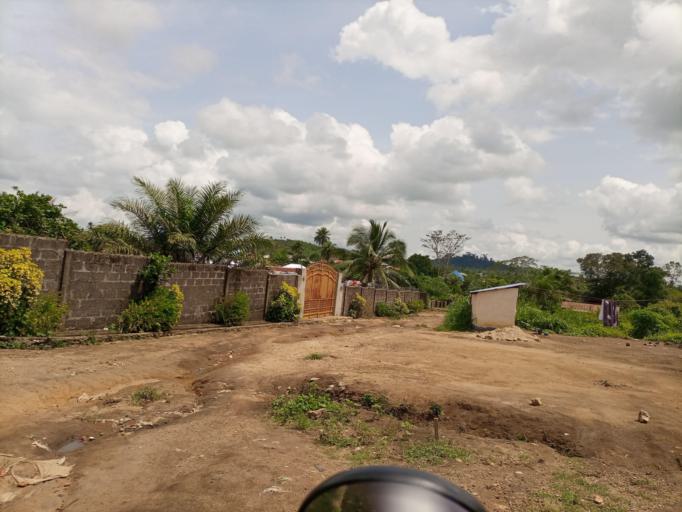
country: SL
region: Southern Province
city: Bo
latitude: 7.9769
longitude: -11.7654
